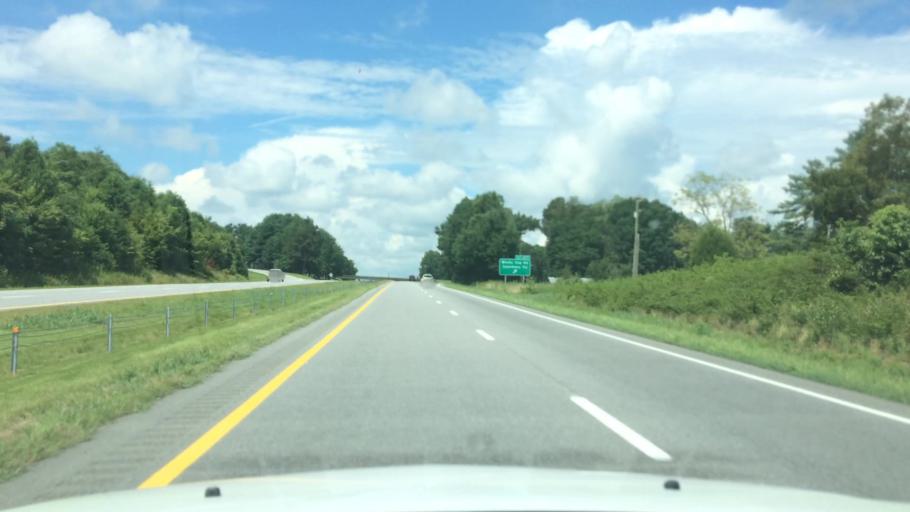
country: US
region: North Carolina
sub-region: Wilkes County
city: North Wilkesboro
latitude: 36.1507
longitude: -81.0124
